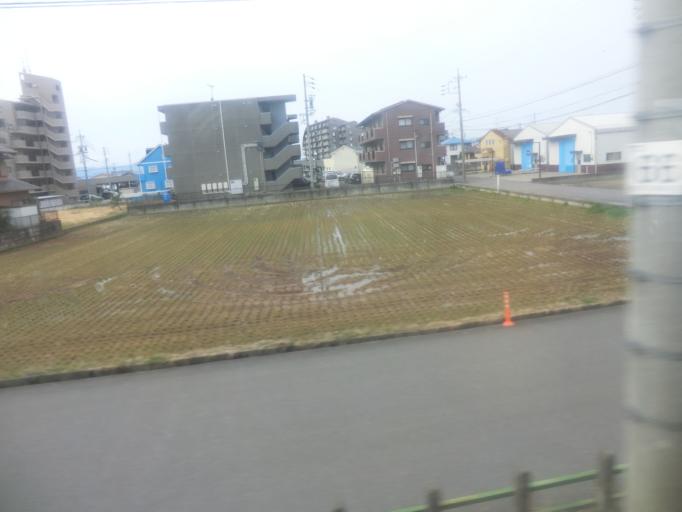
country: JP
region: Aichi
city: Kuroda
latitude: 35.3395
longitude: 136.7814
